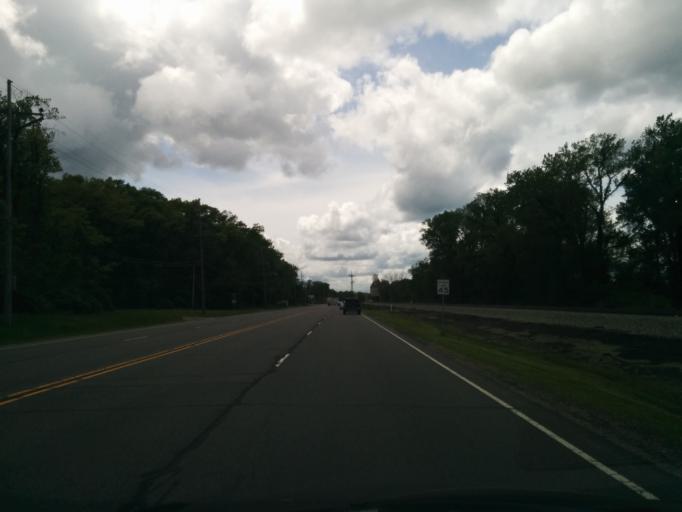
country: US
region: Indiana
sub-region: LaPorte County
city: Long Beach
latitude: 41.7286
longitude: -86.8679
